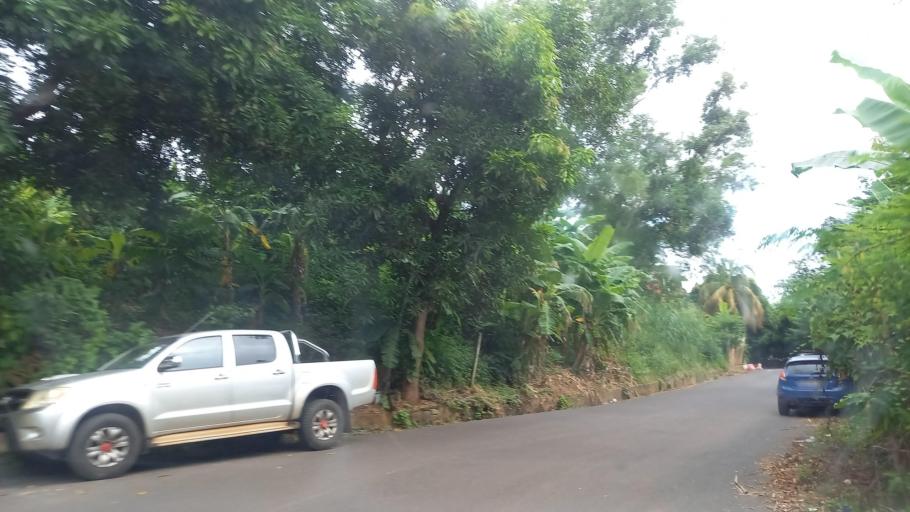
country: YT
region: Boueni
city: Boueni
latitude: -12.9068
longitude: 45.0815
